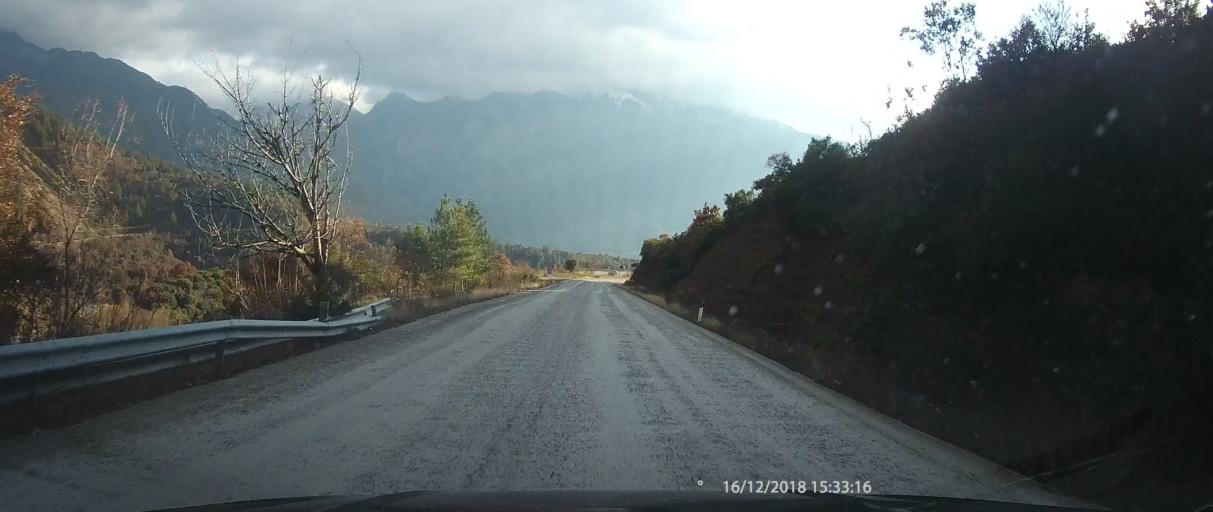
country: GR
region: Epirus
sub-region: Nomos Ioanninon
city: Konitsa
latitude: 40.0648
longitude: 20.7364
